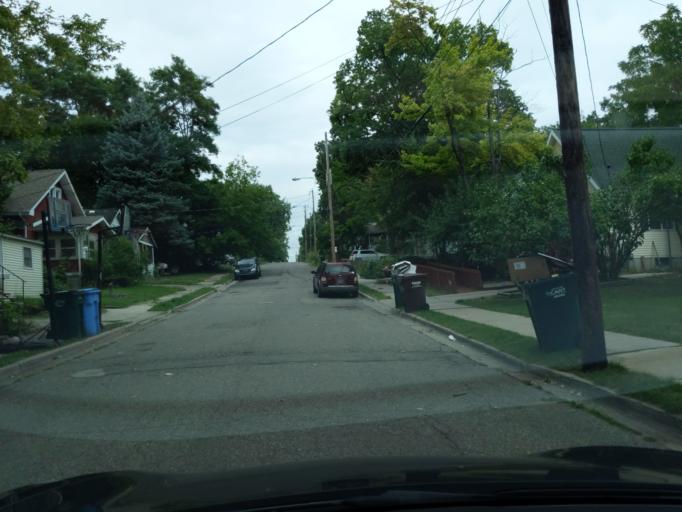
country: US
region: Michigan
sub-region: Ingham County
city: Lansing
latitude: 42.7197
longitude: -84.5286
